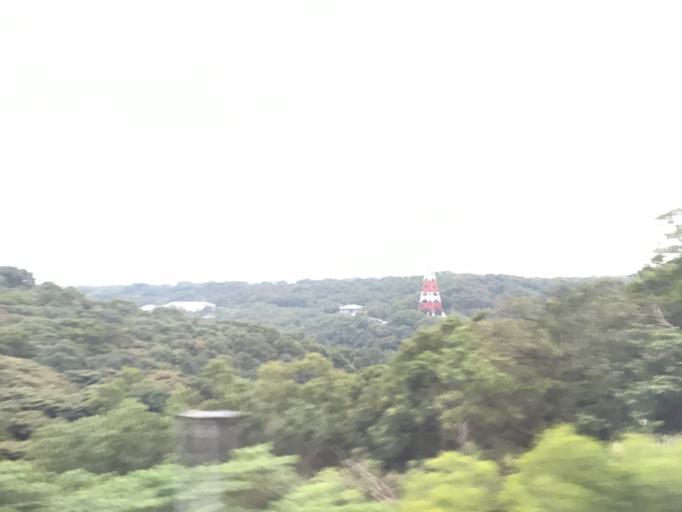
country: TW
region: Taiwan
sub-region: Taoyuan
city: Taoyuan
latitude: 25.0640
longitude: 121.3407
